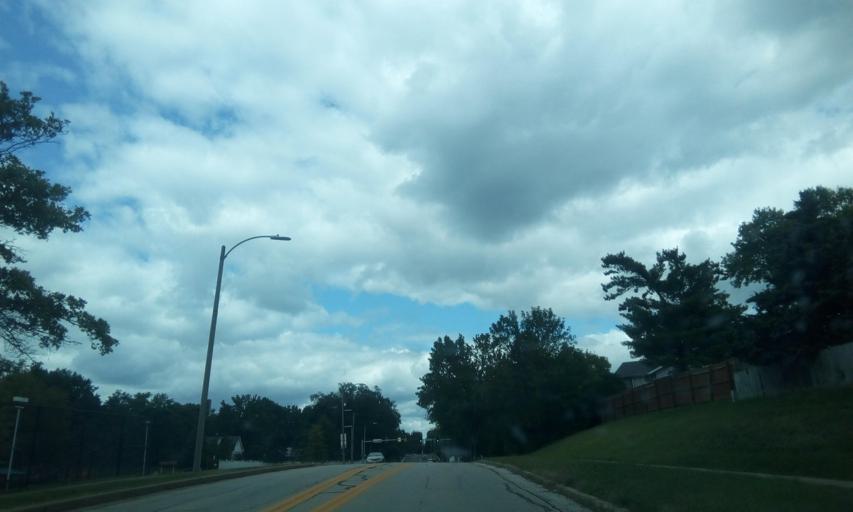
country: US
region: Missouri
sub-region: Saint Louis County
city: Ballwin
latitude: 38.6081
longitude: -90.5385
